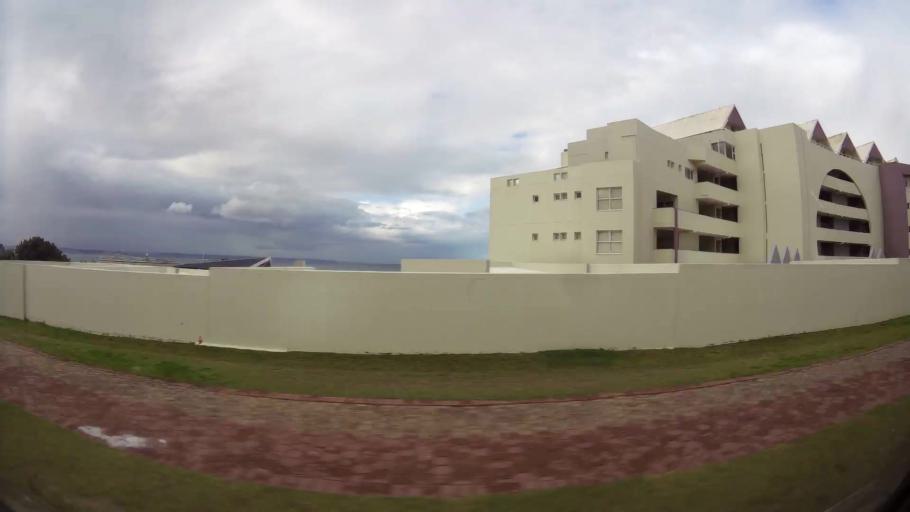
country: ZA
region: Western Cape
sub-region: Eden District Municipality
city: Mossel Bay
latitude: -34.1607
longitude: 22.1095
